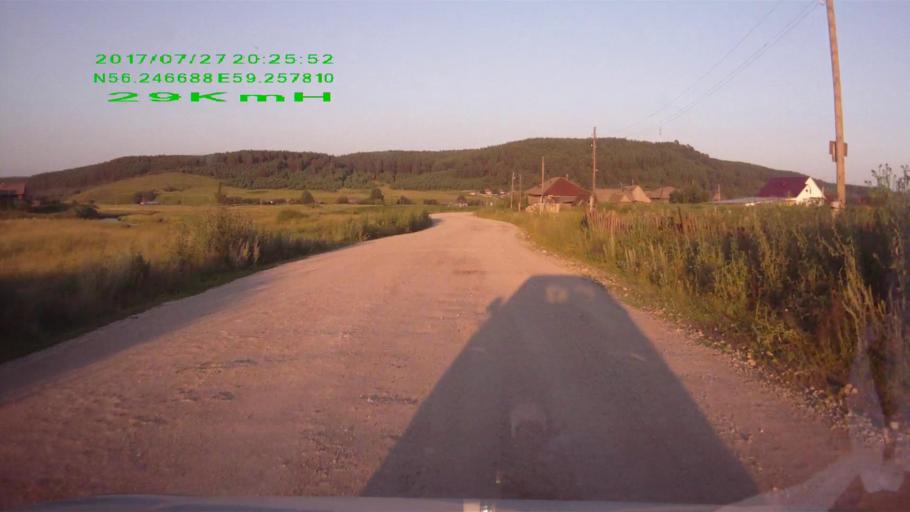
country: RU
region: Sverdlovsk
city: Mikhaylovsk
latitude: 56.2467
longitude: 59.2593
